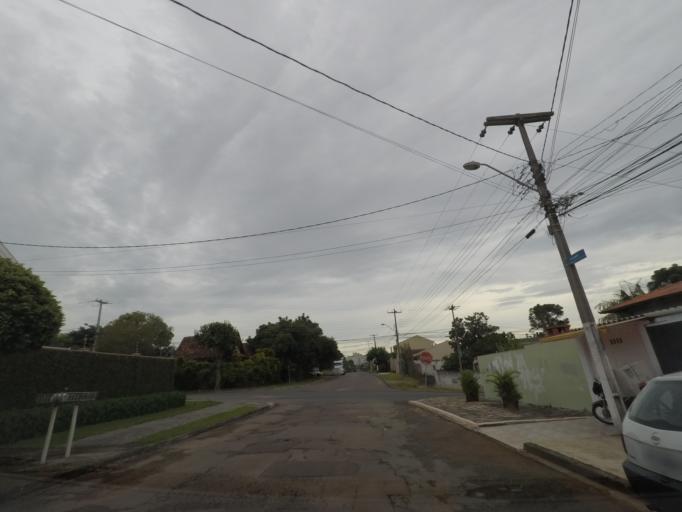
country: BR
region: Parana
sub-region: Curitiba
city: Curitiba
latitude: -25.4664
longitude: -49.3026
